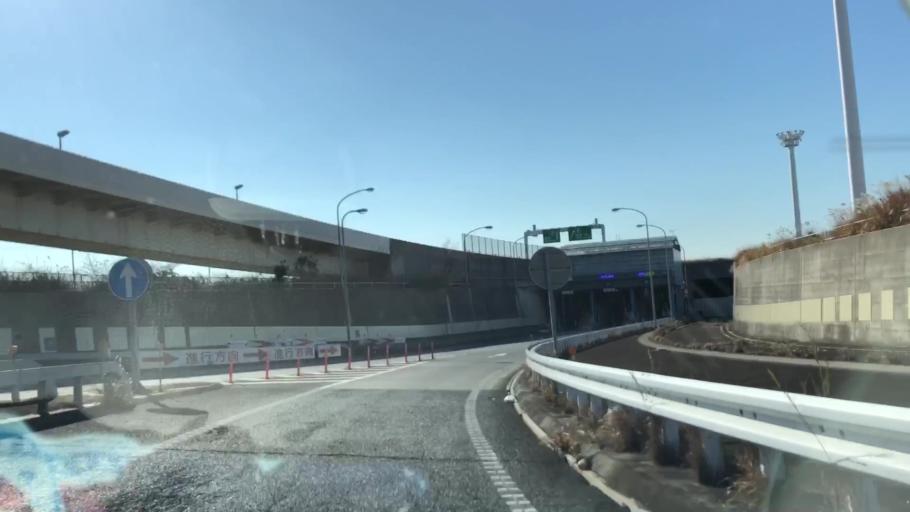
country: JP
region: Kanagawa
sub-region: Kawasaki-shi
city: Kawasaki
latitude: 35.5158
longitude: 139.7913
